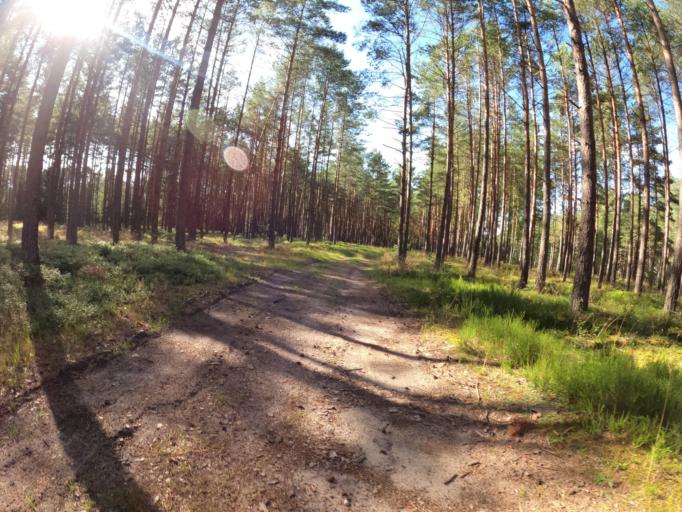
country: PL
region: West Pomeranian Voivodeship
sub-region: Powiat bialogardzki
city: Tychowo
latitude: 54.0492
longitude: 16.3097
